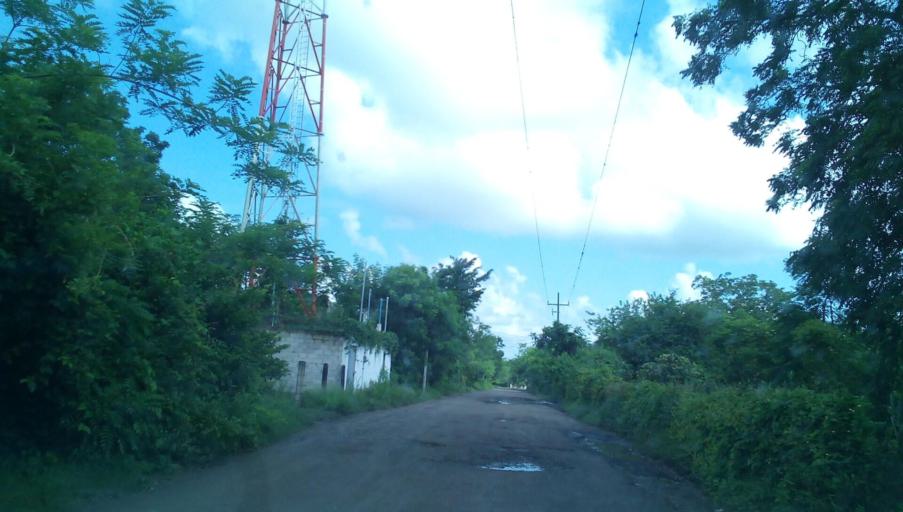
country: MX
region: Veracruz
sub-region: Citlaltepetl
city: Las Sabinas
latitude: 21.3647
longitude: -97.9004
